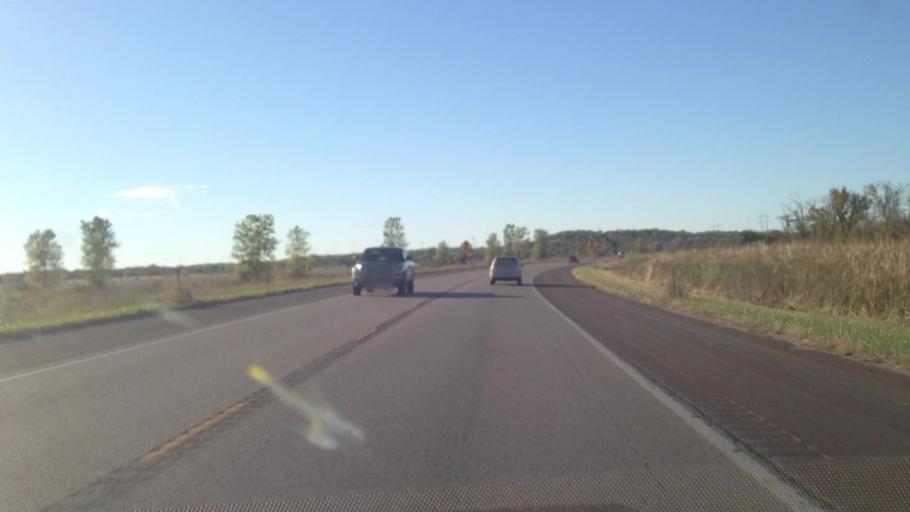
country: US
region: Kansas
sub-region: Douglas County
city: Lawrence
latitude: 38.9306
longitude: -95.2996
